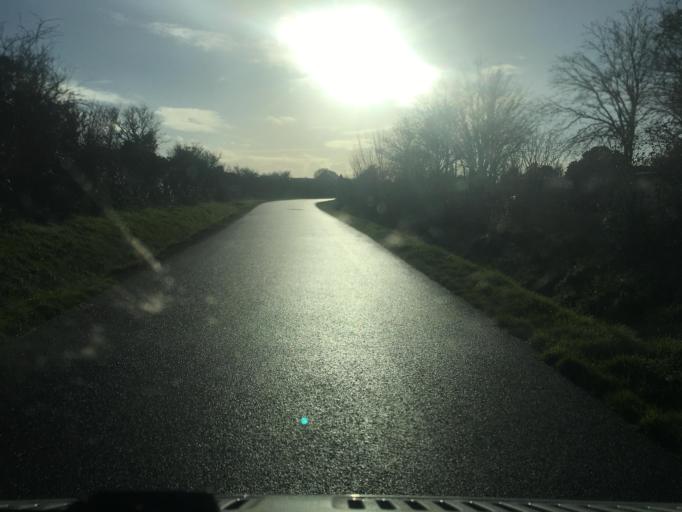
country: FR
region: Brittany
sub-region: Departement du Morbihan
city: Surzur
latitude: 47.5121
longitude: -2.6764
